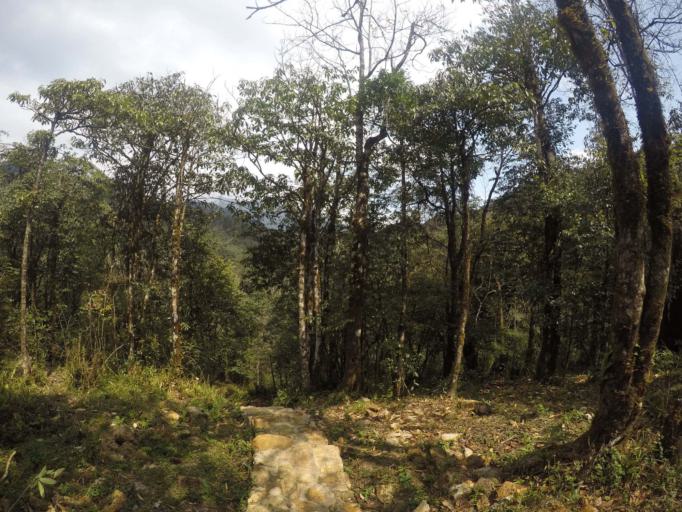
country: VN
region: Lao Cai
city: Sa Pa
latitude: 22.3498
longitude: 103.7743
